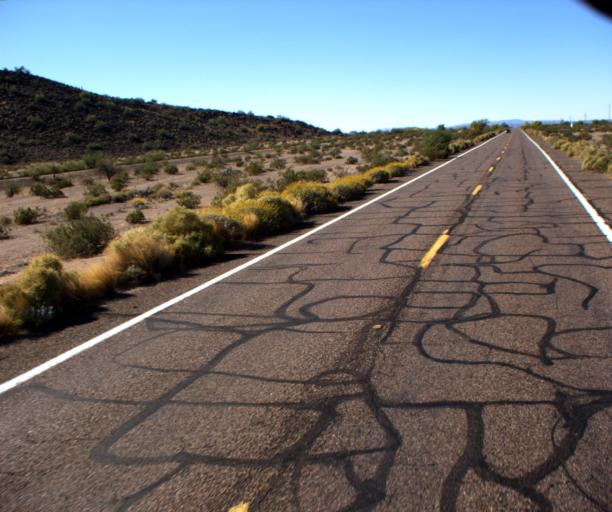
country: US
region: Arizona
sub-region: Maricopa County
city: Gila Bend
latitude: 32.7556
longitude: -112.8242
